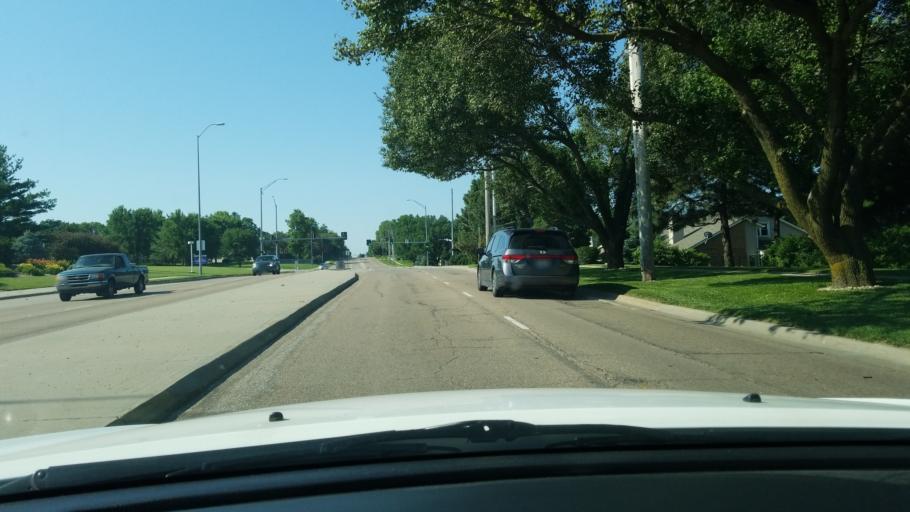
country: US
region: Nebraska
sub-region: Lancaster County
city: Lincoln
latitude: 40.8002
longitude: -96.6061
